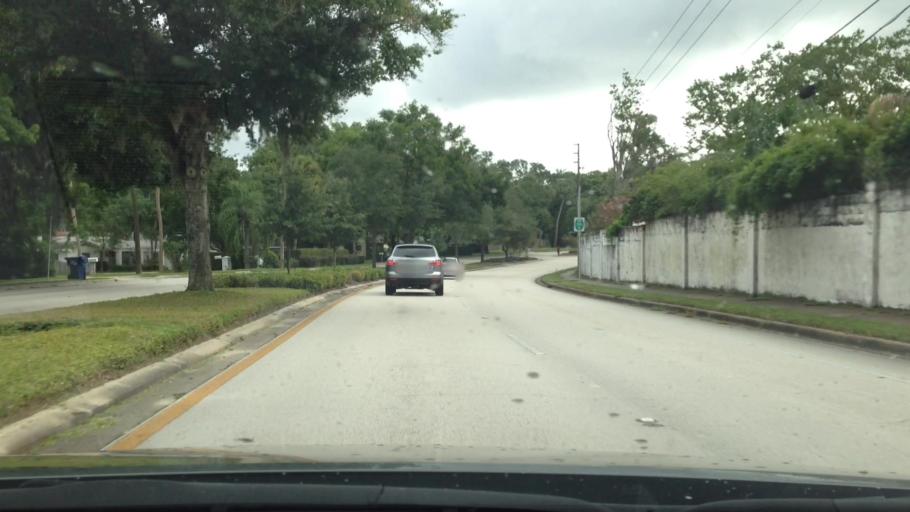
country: US
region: Florida
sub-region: Orange County
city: Maitland
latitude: 28.6281
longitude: -81.3498
